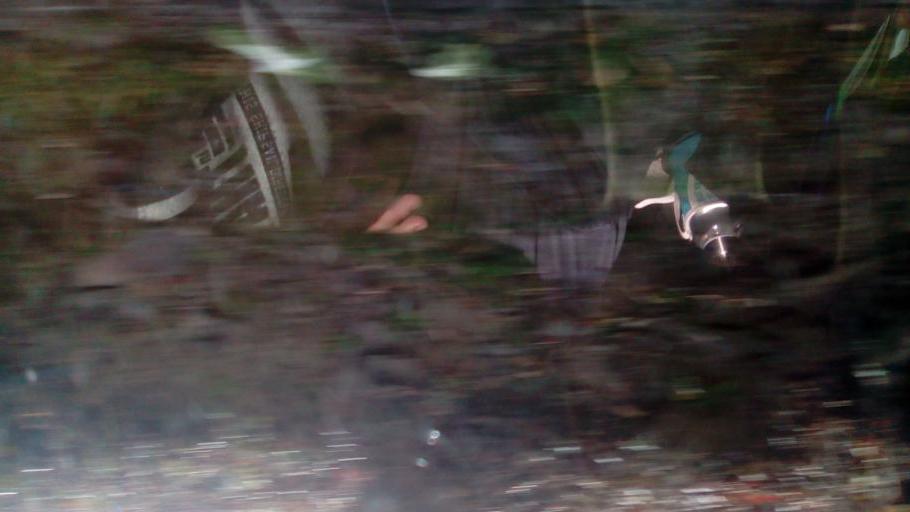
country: TW
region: Taiwan
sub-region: Hualien
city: Hualian
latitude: 24.3617
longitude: 121.3317
